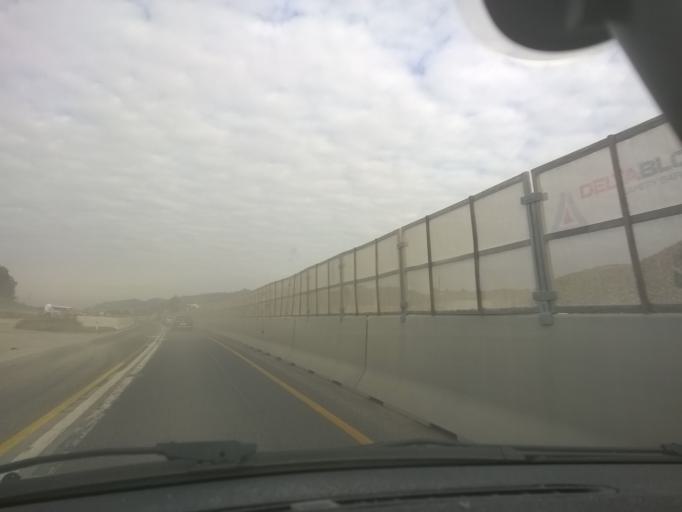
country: SI
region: Podlehnik
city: Podlehnik
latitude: 46.3274
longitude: 15.8792
